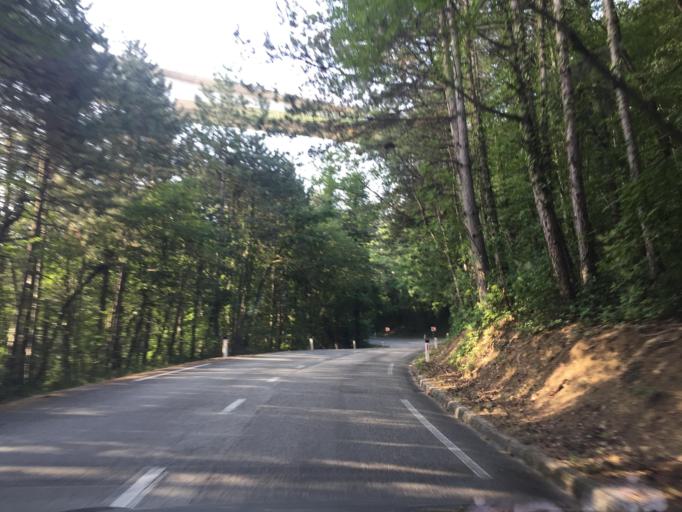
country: IT
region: Friuli Venezia Giulia
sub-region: Provincia di Trieste
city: Dolina
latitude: 45.5562
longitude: 13.8674
